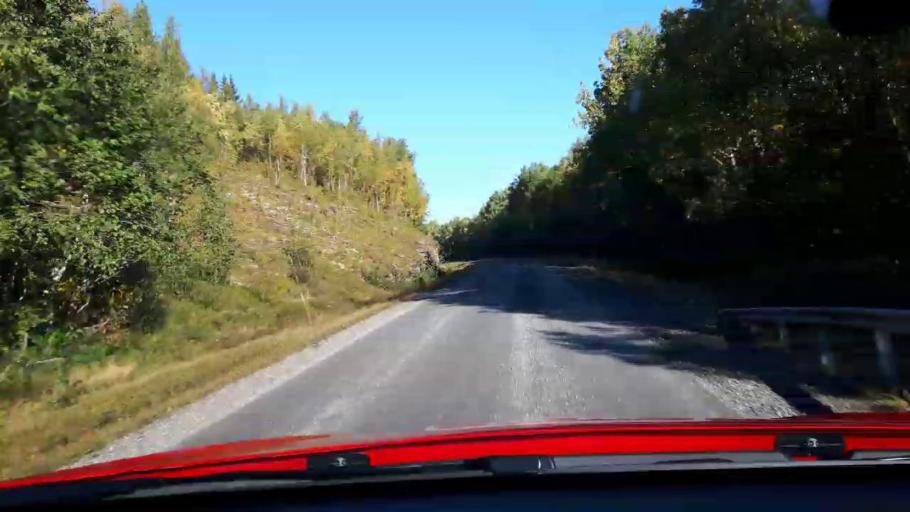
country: NO
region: Nord-Trondelag
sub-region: Lierne
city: Sandvika
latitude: 64.5712
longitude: 13.9028
